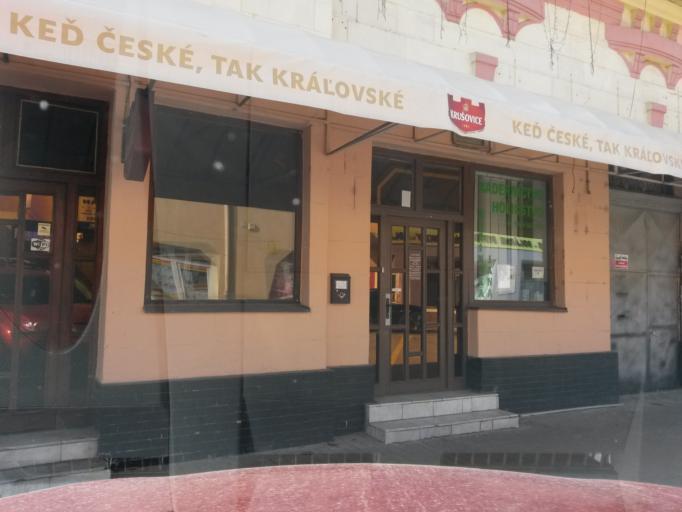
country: SK
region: Banskobystricky
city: Lucenec
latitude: 48.3347
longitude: 19.6669
